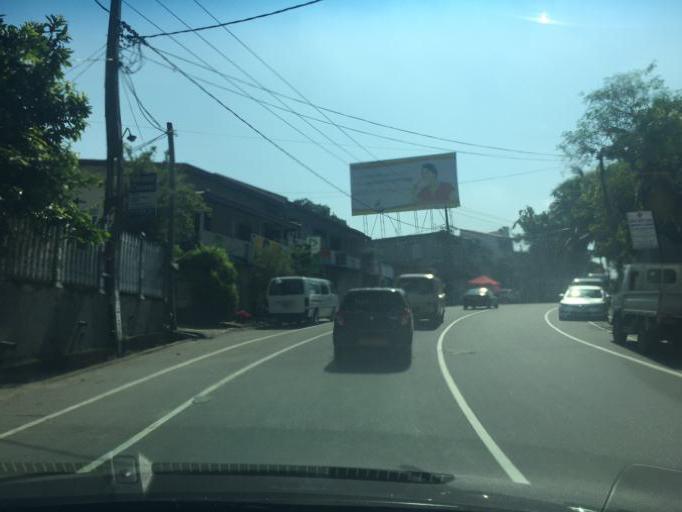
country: LK
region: Western
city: Sri Jayewardenepura Kotte
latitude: 6.8569
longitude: 79.8930
